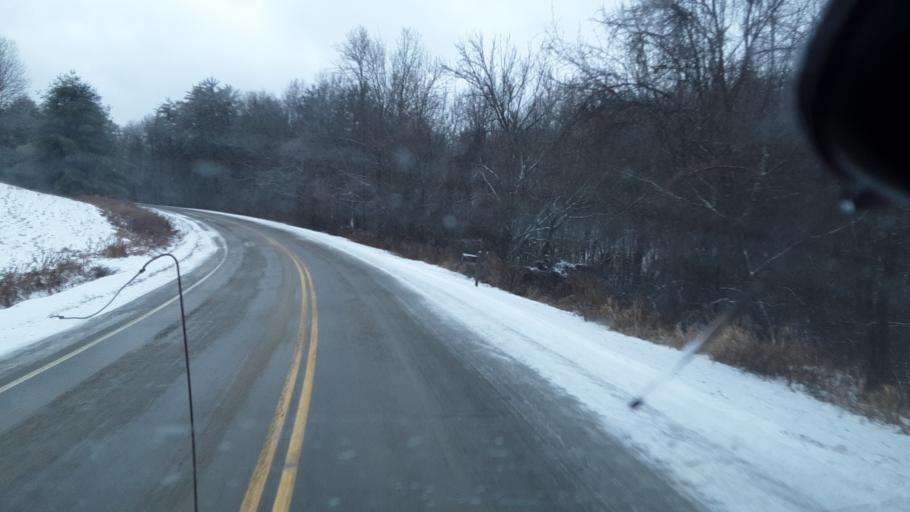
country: US
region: New York
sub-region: Allegany County
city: Friendship
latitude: 42.2450
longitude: -78.1473
